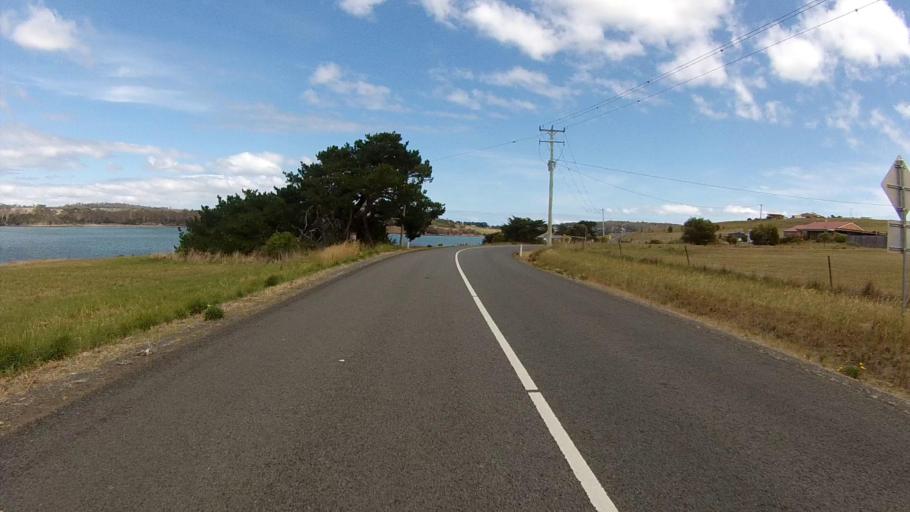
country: AU
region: Tasmania
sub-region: Sorell
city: Sorell
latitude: -42.8661
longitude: 147.6763
